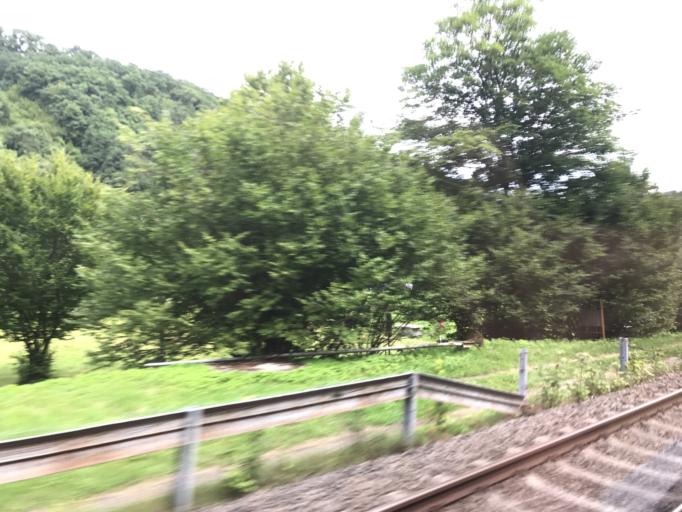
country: DE
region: Rheinland-Pfalz
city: Gutenacker
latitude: 50.3284
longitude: 7.9308
